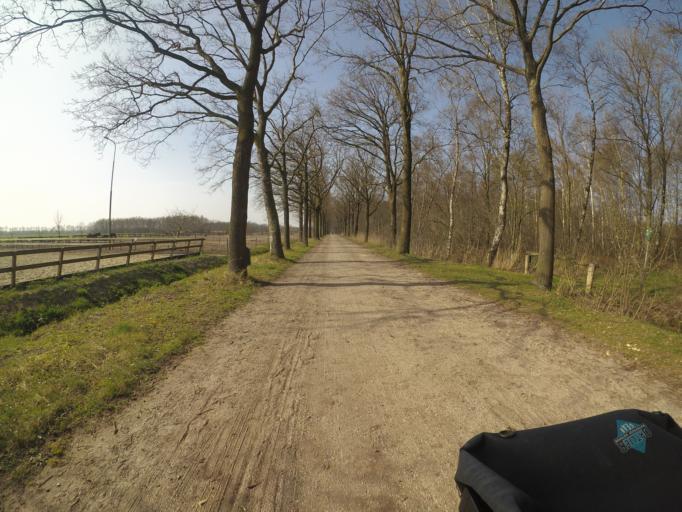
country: NL
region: North Brabant
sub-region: Gemeente Maasdonk
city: Geffen
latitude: 51.6878
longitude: 5.4386
